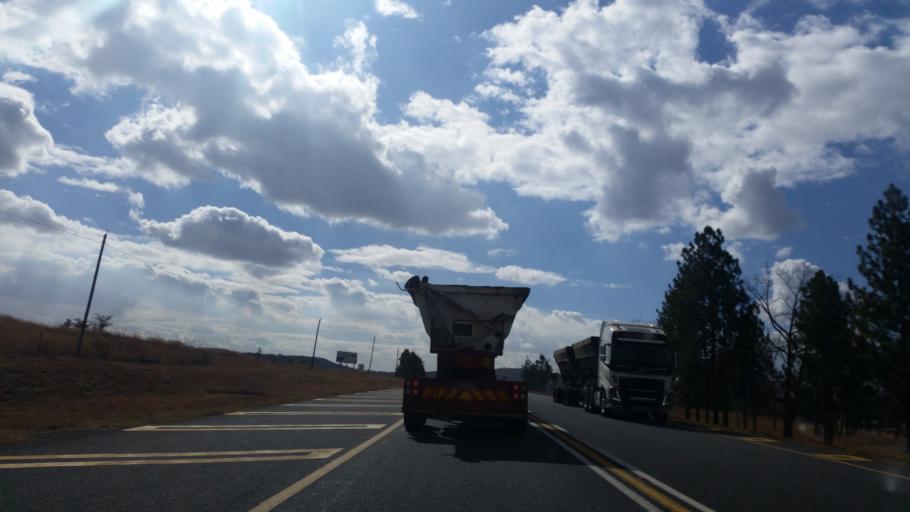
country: ZA
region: KwaZulu-Natal
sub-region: Amajuba District Municipality
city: Newcastle
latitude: -27.8368
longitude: 29.9609
